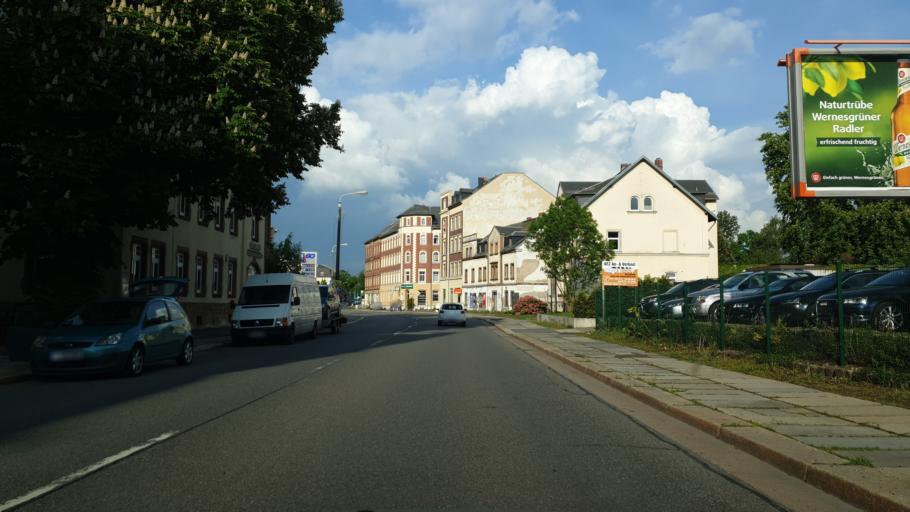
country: DE
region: Saxony
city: Neukirchen
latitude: 50.8210
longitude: 12.8845
